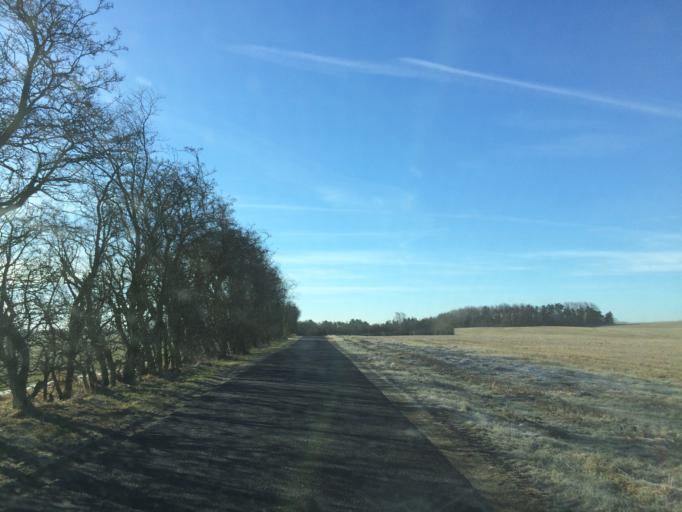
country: DK
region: North Denmark
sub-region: Mariagerfjord Kommune
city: Hobro
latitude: 56.6215
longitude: 9.6442
